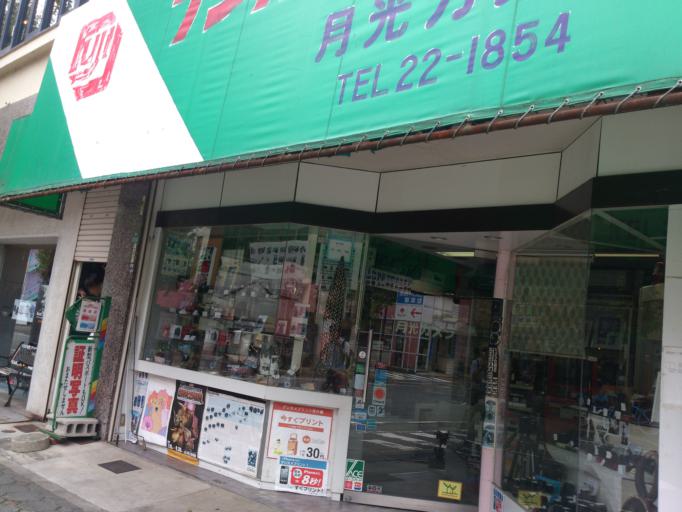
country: JP
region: Yamaguchi
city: Yamaguchi-shi
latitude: 34.1757
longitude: 131.4775
